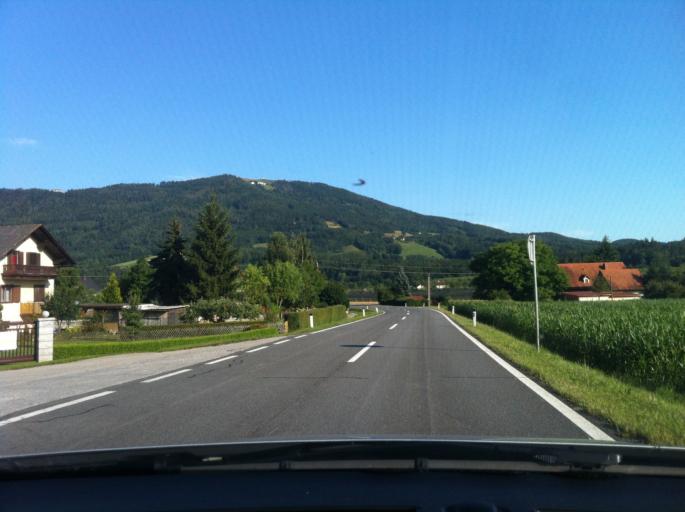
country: AT
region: Styria
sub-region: Politischer Bezirk Weiz
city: Floing
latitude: 47.2465
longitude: 15.7316
